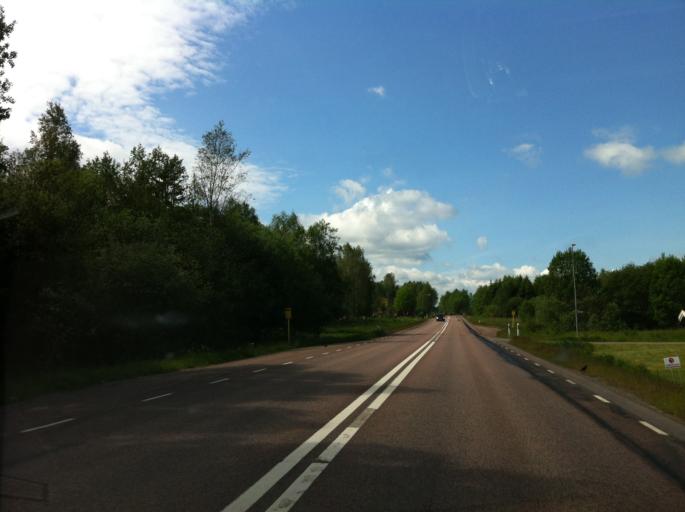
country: SE
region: Vaermland
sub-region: Karlstads Kommun
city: Valberg
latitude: 59.3783
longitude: 13.1602
